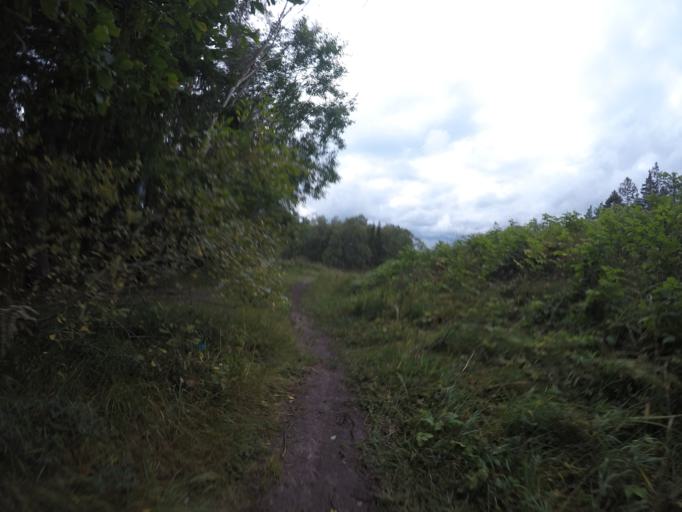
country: SE
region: Vaestmanland
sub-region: Vasteras
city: Vasteras
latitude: 59.6442
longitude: 16.5143
